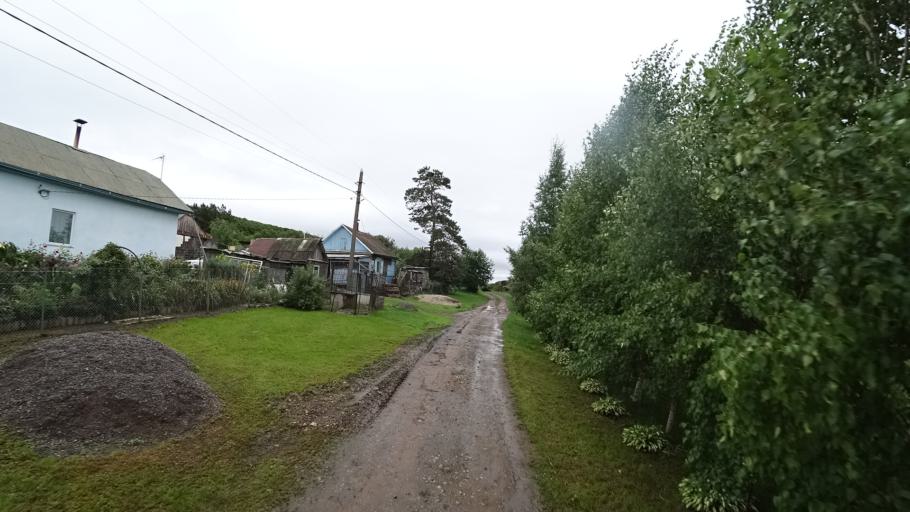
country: RU
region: Primorskiy
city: Monastyrishche
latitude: 44.2707
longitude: 132.4045
